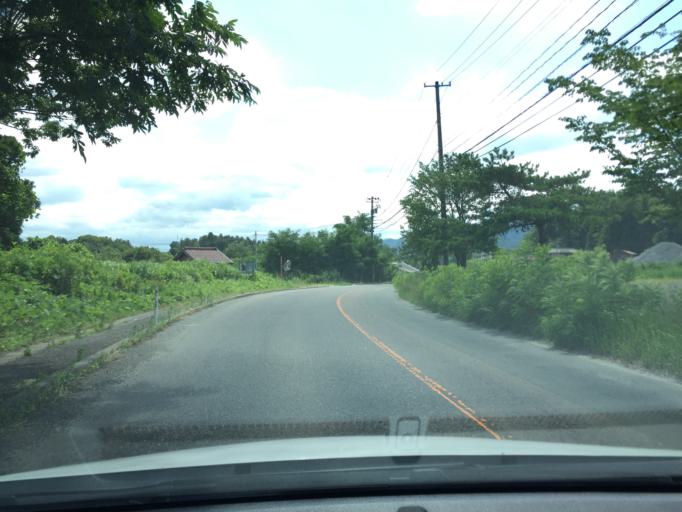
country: JP
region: Fukushima
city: Koriyama
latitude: 37.3635
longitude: 140.2937
